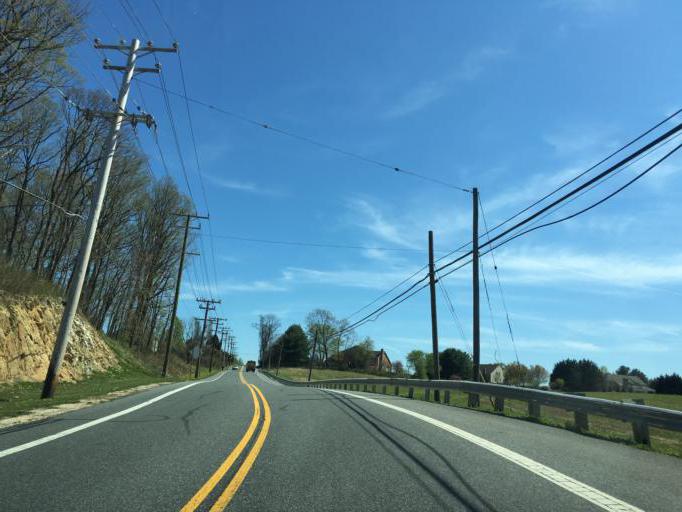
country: US
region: Maryland
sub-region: Baltimore County
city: Hunt Valley
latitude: 39.5599
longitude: -76.6559
